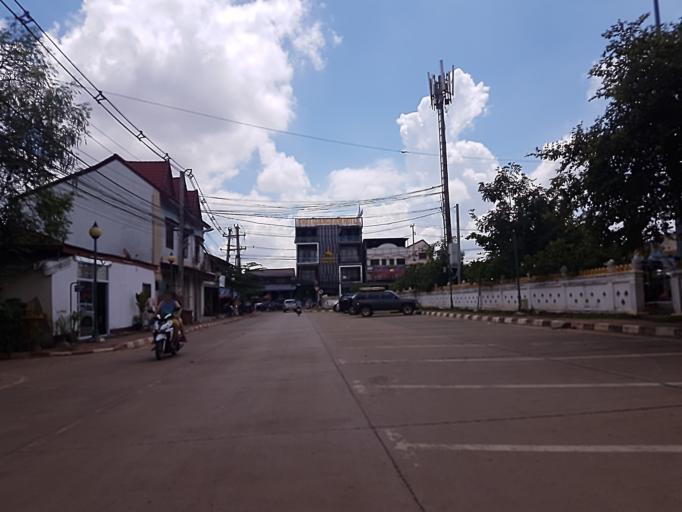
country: LA
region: Vientiane
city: Vientiane
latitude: 17.9760
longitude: 102.6375
